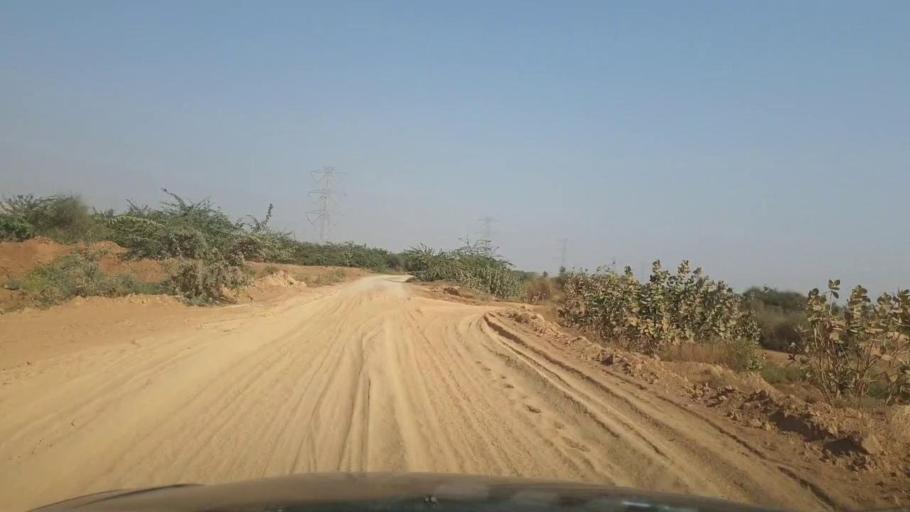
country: PK
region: Sindh
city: Gharo
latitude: 25.2310
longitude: 67.6782
